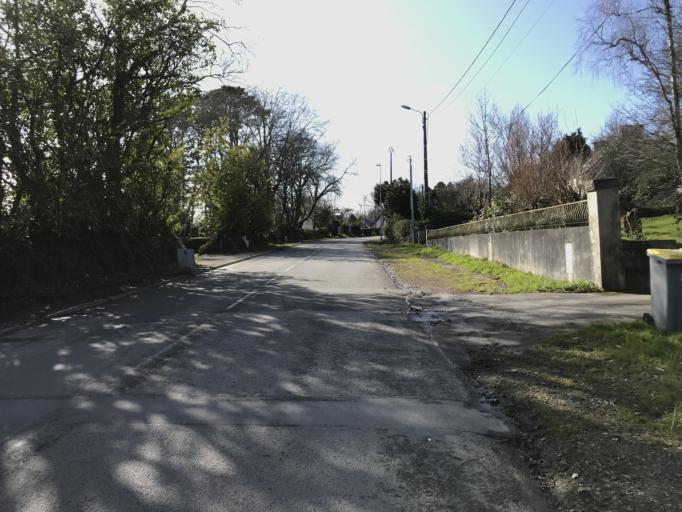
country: FR
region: Brittany
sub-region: Departement du Finistere
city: Plougastel-Daoulas
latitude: 48.3813
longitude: -4.3436
